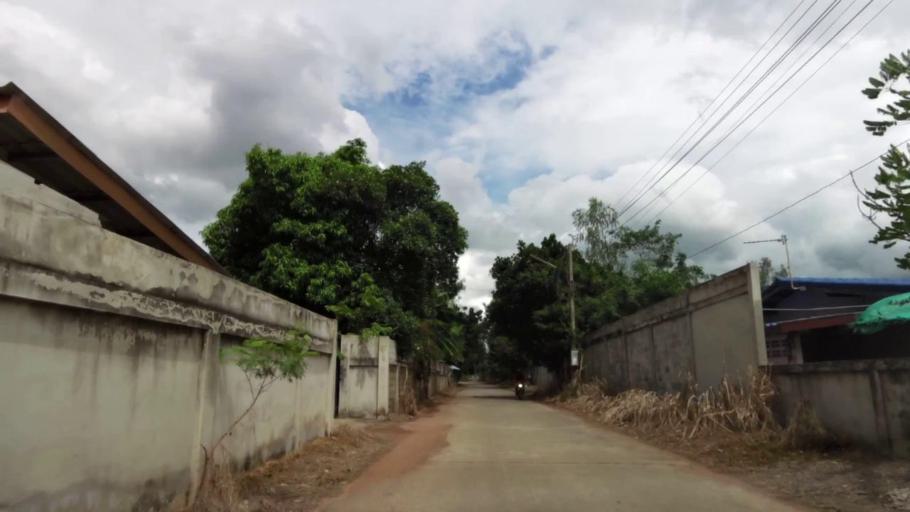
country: TH
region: Nakhon Sawan
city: Phai Sali
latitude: 15.5937
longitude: 100.6537
